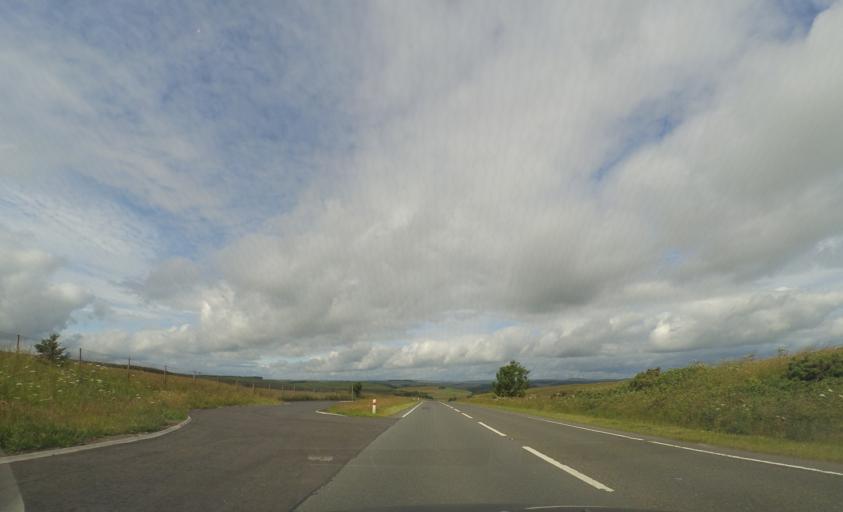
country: GB
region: Scotland
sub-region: The Scottish Borders
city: Hawick
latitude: 55.4731
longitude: -2.7990
